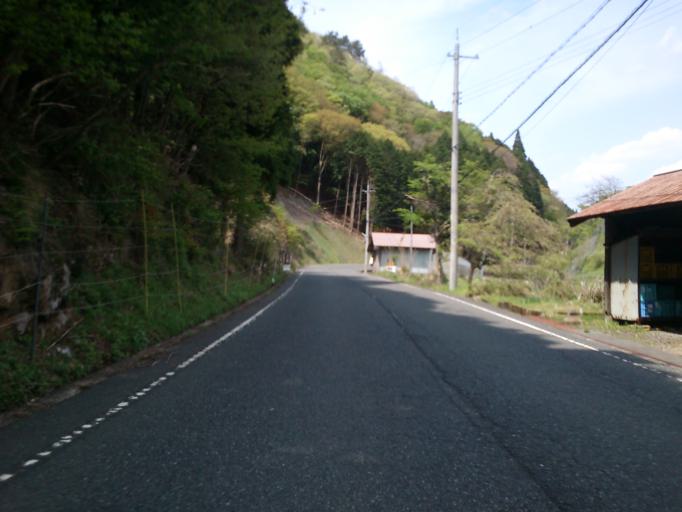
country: JP
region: Hyogo
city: Toyooka
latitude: 35.3972
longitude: 134.9459
